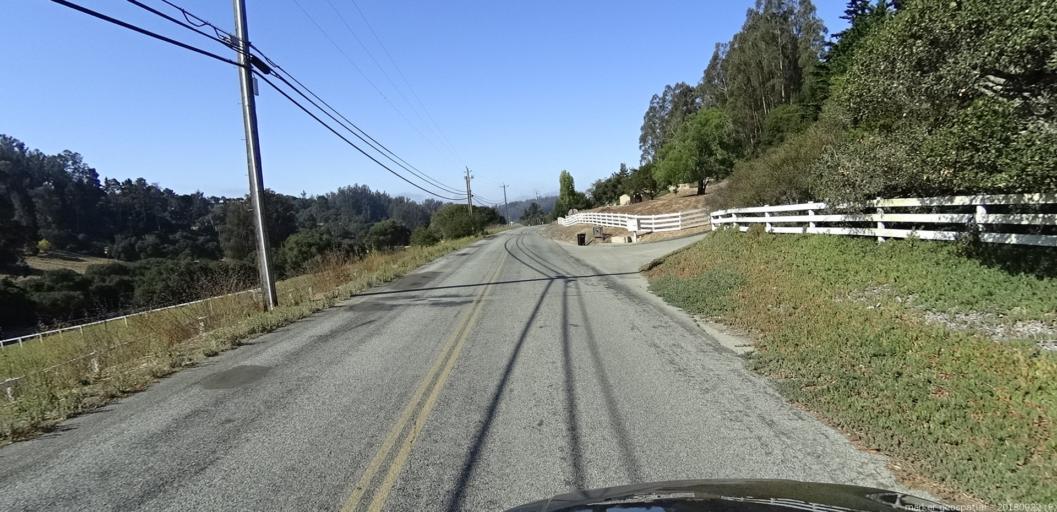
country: US
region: California
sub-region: Monterey County
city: Prunedale
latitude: 36.8050
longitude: -121.6529
